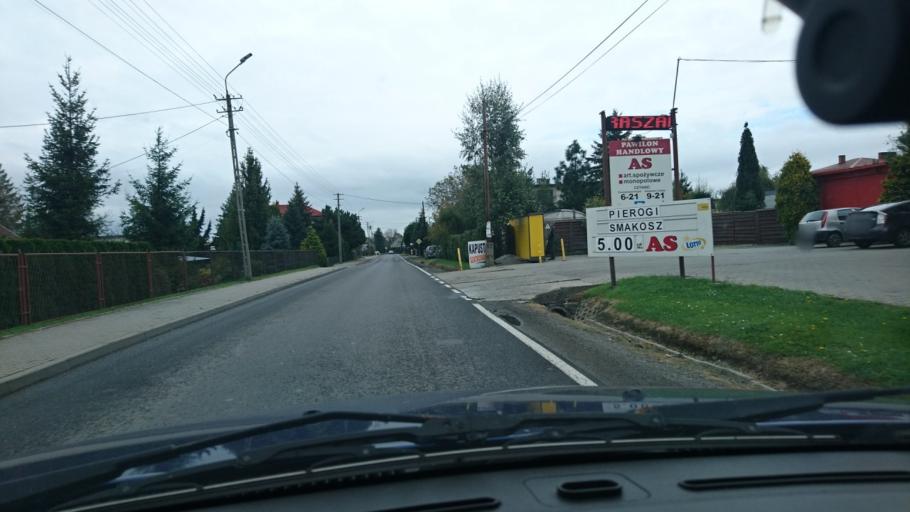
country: PL
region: Silesian Voivodeship
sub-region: Powiat bielski
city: Kozy
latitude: 49.8514
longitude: 19.1427
